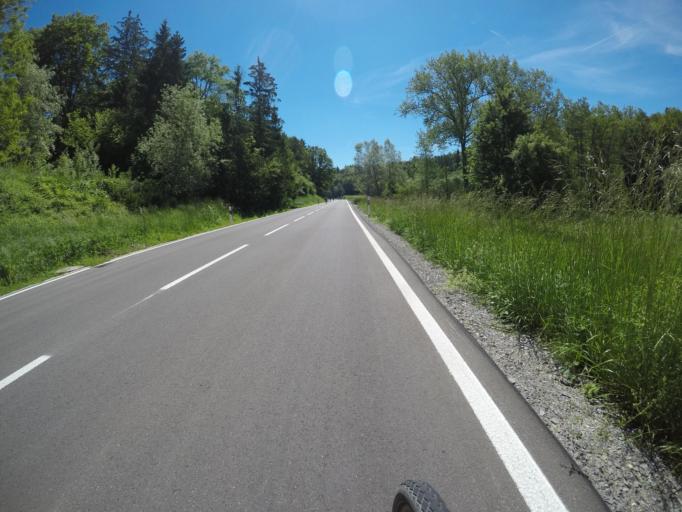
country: DE
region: Baden-Wuerttemberg
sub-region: Karlsruhe Region
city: Neuhausen
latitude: 48.8064
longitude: 8.8118
